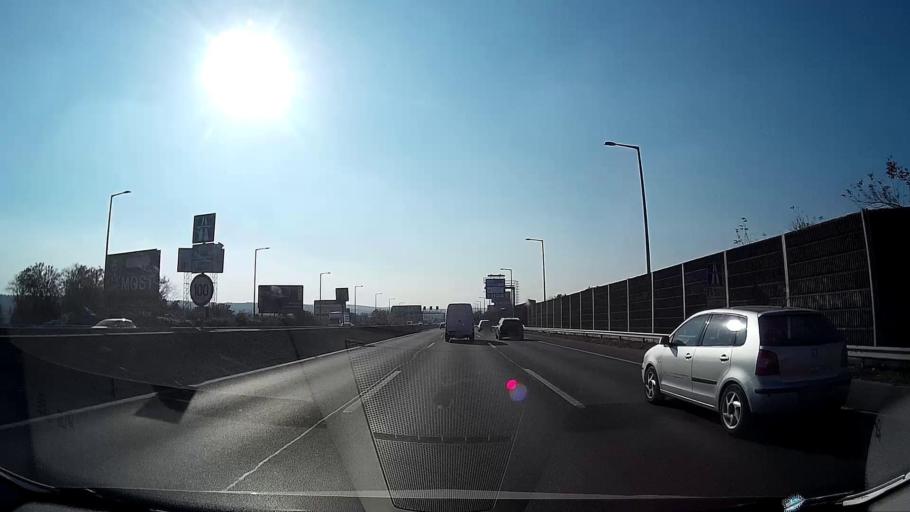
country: HU
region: Pest
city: Budaors
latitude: 47.4585
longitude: 18.9818
